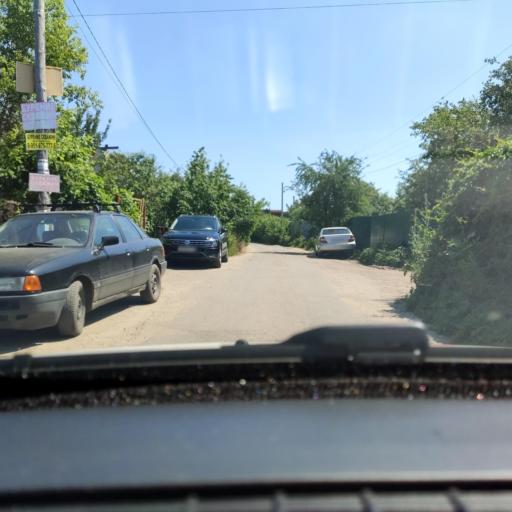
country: RU
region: Voronezj
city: Shilovo
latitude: 51.5890
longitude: 39.1527
